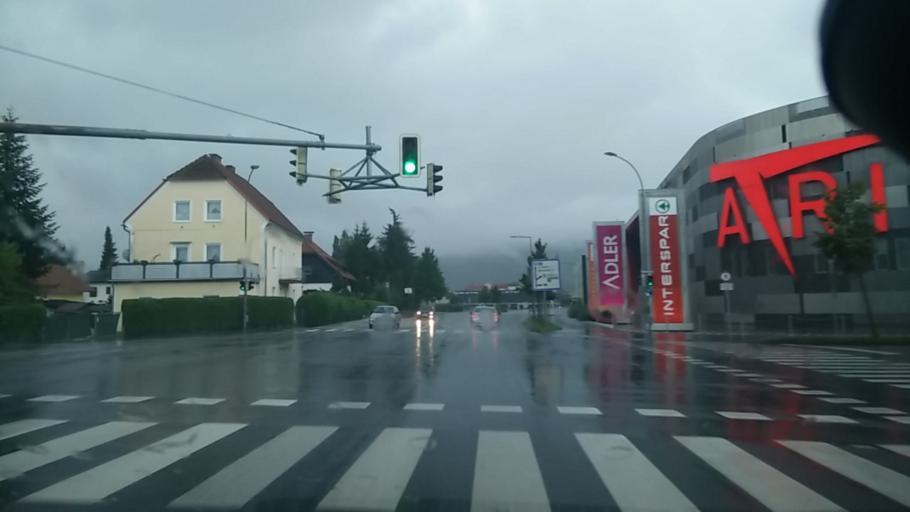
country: AT
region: Carinthia
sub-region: Villach Stadt
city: Villach
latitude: 46.5968
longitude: 13.8382
